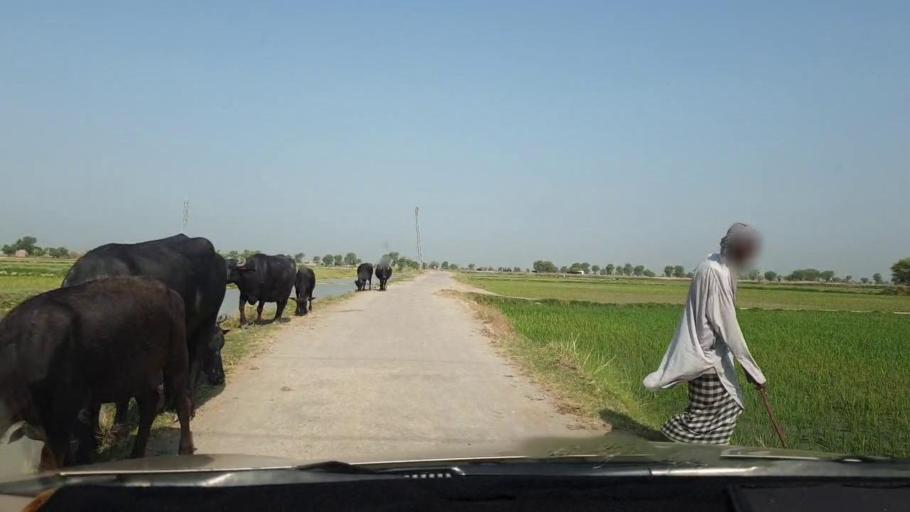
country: PK
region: Sindh
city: Larkana
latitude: 27.6401
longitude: 68.2336
